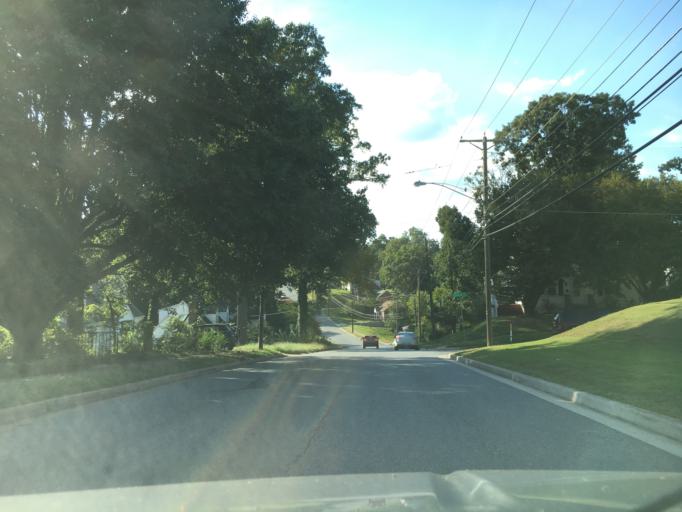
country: US
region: Virginia
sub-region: City of Lynchburg
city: West Lynchburg
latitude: 37.3848
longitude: -79.1803
